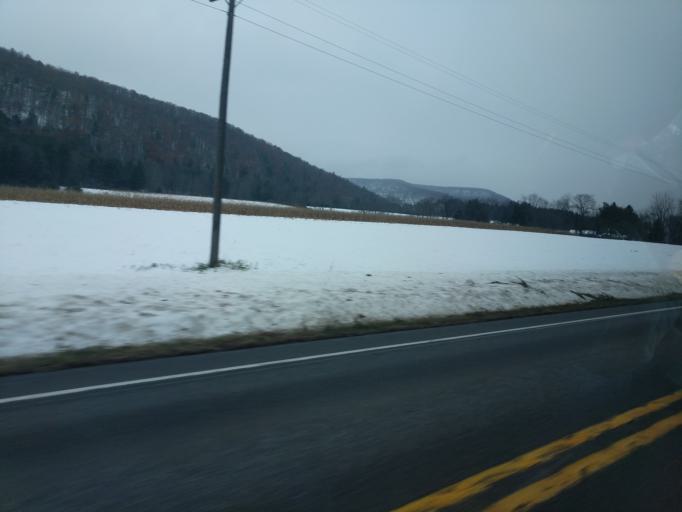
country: US
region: Pennsylvania
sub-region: Tioga County
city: Wellsboro
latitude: 41.8508
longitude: -77.2511
